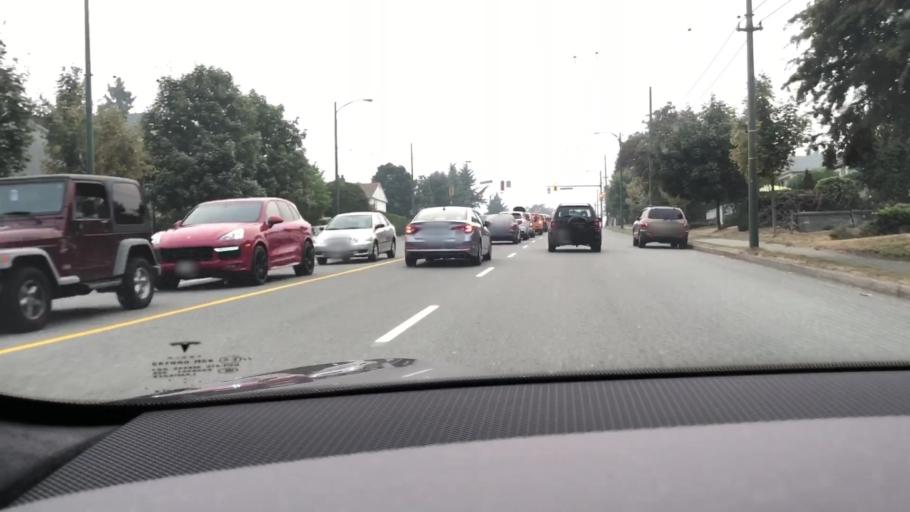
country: CA
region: British Columbia
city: Vancouver
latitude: 49.2332
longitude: -123.1039
